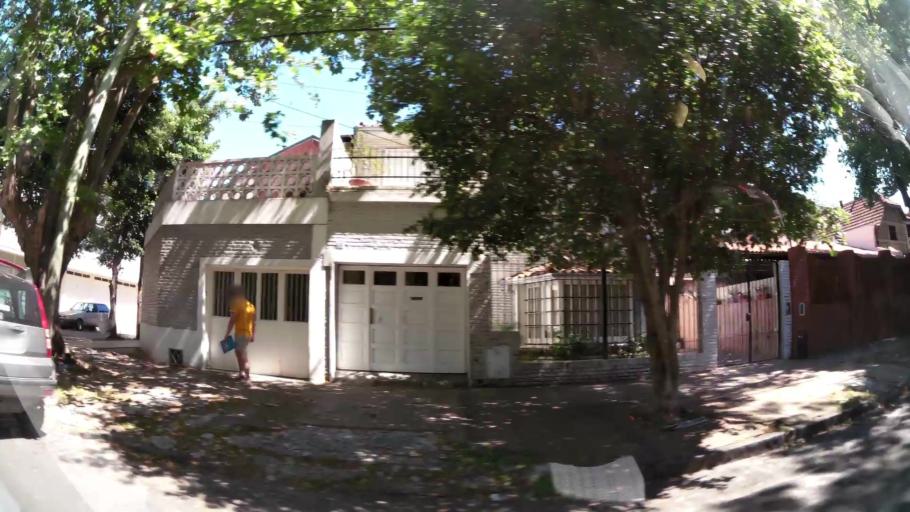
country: AR
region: Buenos Aires
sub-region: Partido de Vicente Lopez
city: Olivos
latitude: -34.5341
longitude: -58.4974
